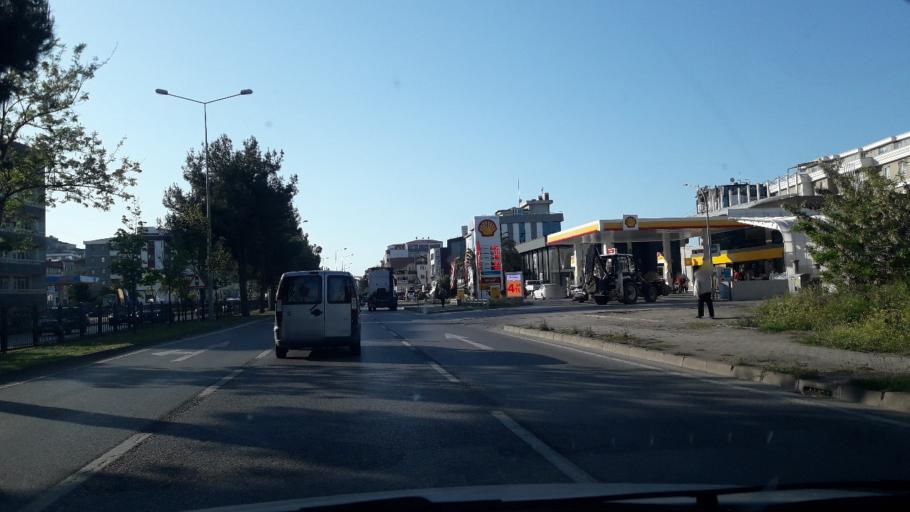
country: TR
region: Samsun
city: Taflan
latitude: 41.3584
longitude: 36.2352
